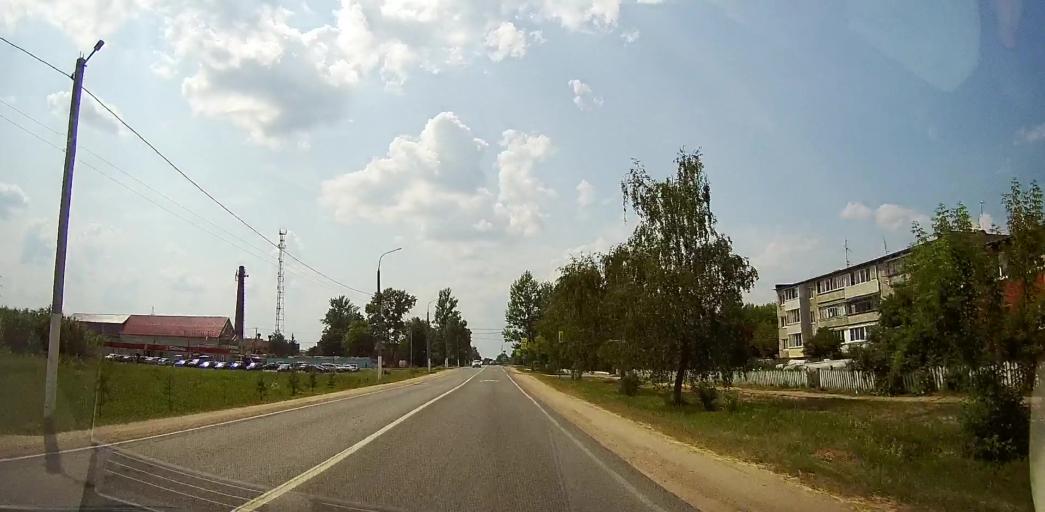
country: RU
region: Moskovskaya
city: Malino
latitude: 55.1040
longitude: 38.1789
